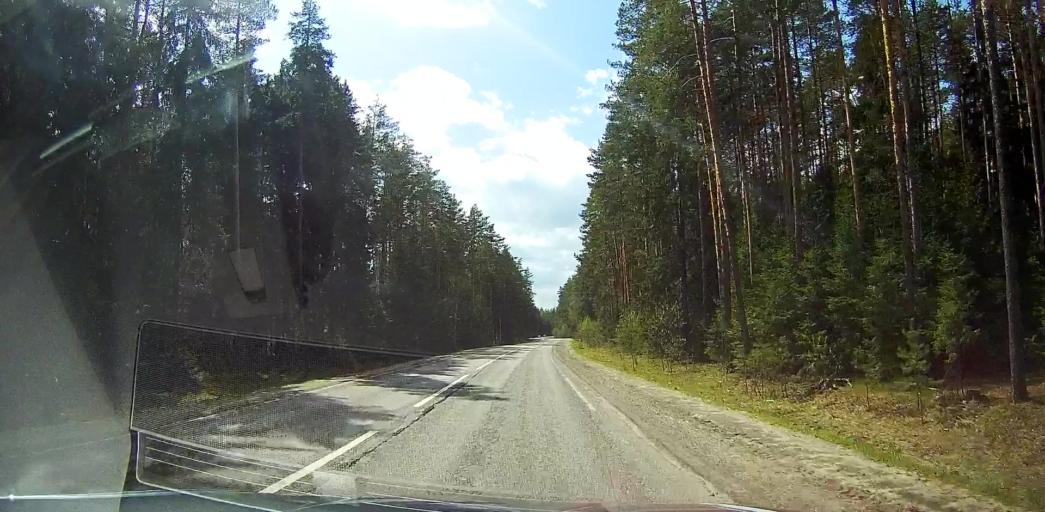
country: RU
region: Moskovskaya
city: Davydovo
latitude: 55.5602
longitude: 38.8442
